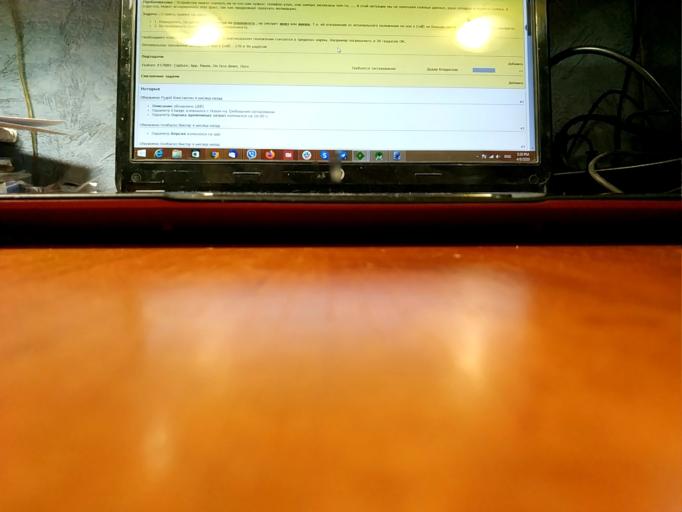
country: RU
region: Tverskaya
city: Sandovo
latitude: 58.6429
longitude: 36.4327
